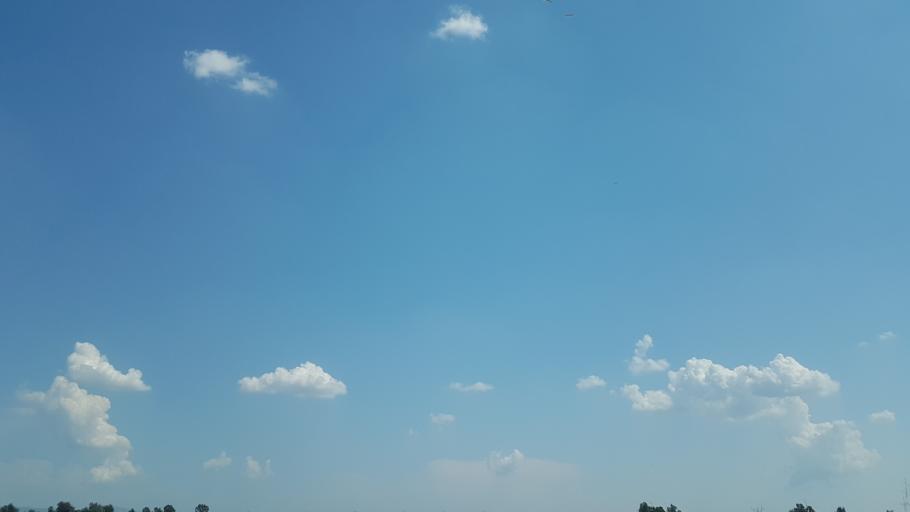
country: TR
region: Adana
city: Yuregir
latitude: 37.0118
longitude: 35.3962
